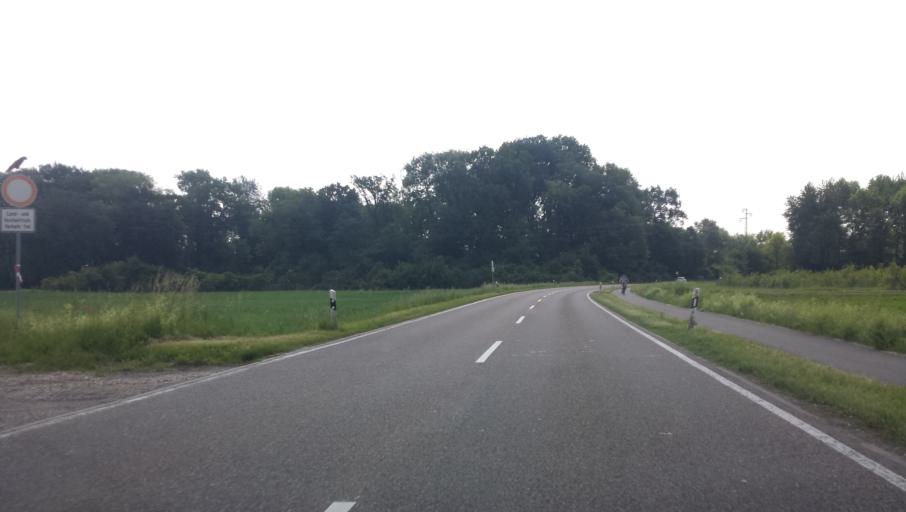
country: DE
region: Rheinland-Pfalz
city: Jockgrim
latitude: 49.0750
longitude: 8.2793
